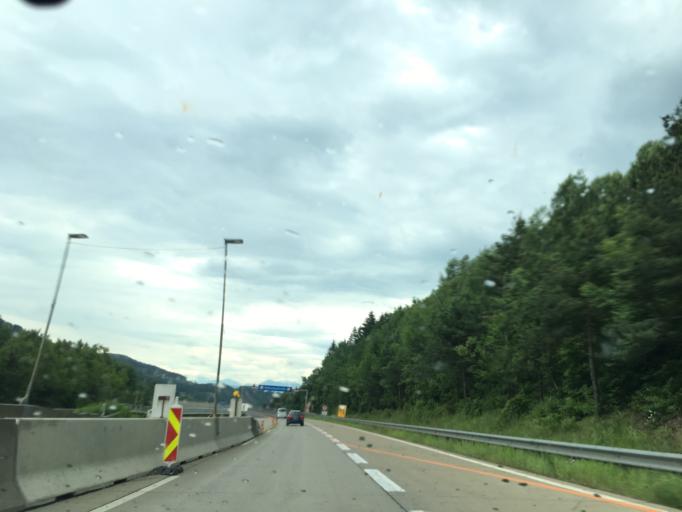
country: AT
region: Carinthia
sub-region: Villach Stadt
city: Villach
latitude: 46.6424
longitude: 13.7993
